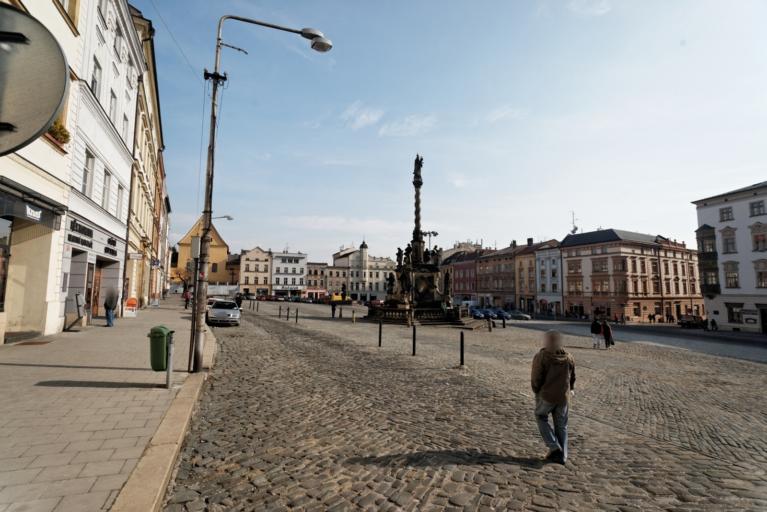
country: CZ
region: Olomoucky
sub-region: Okres Olomouc
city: Olomouc
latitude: 49.5925
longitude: 17.2526
